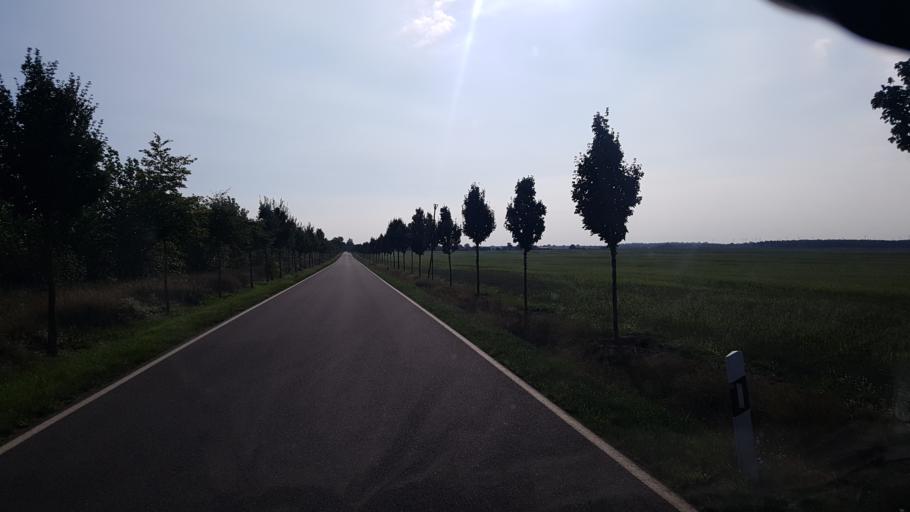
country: DE
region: Brandenburg
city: Luebben
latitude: 51.8830
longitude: 13.8260
